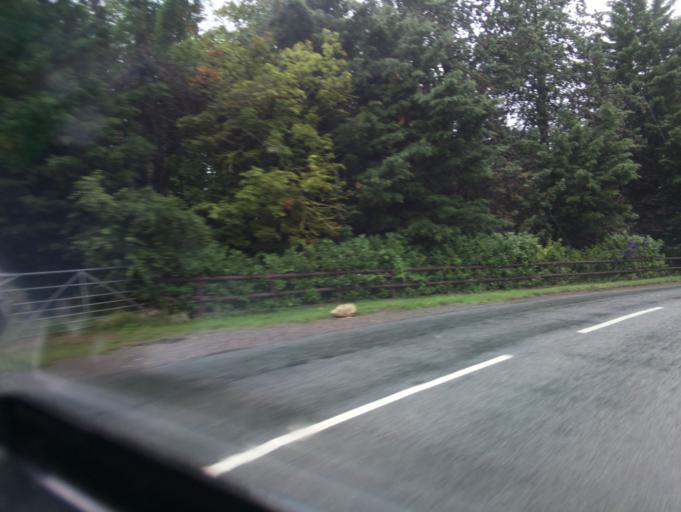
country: GB
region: England
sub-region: Gloucestershire
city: Uckington
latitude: 51.9525
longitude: -2.1242
